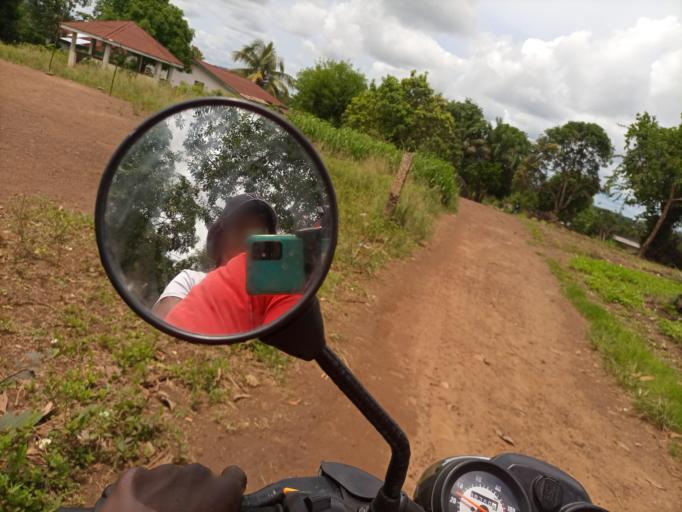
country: SL
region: Southern Province
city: Baoma
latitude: 7.9720
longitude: -11.7129
